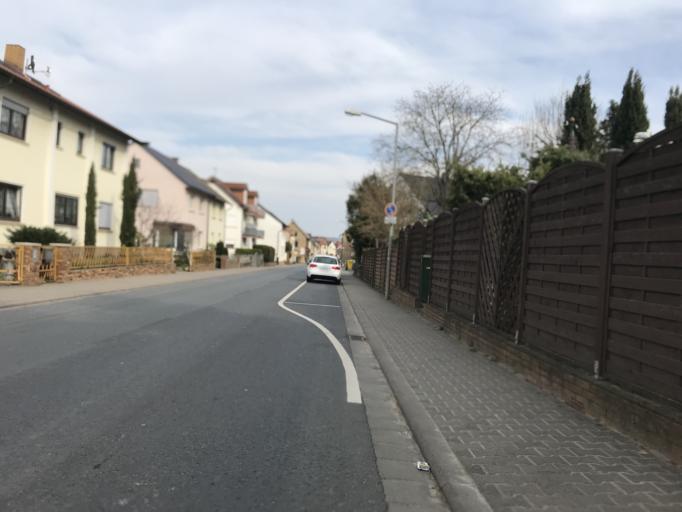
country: DE
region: Rheinland-Pfalz
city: Stadecken-Elsheim
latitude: 49.9096
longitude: 8.1301
